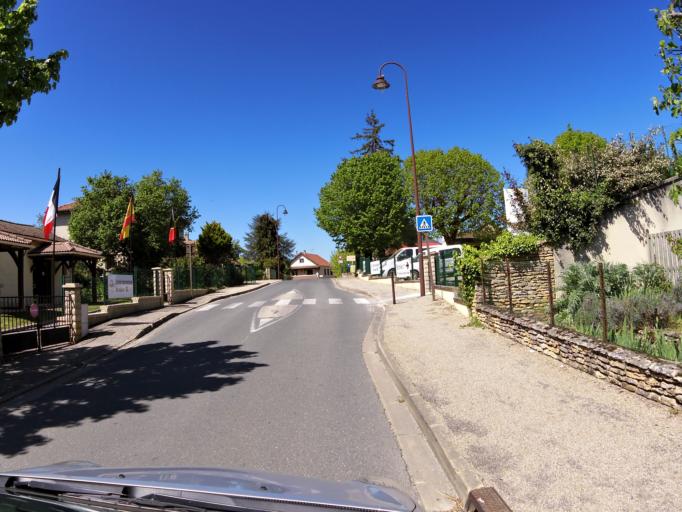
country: FR
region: Aquitaine
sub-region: Departement de la Dordogne
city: Eyvigues-et-Eybenes
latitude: 44.9732
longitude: 1.3217
